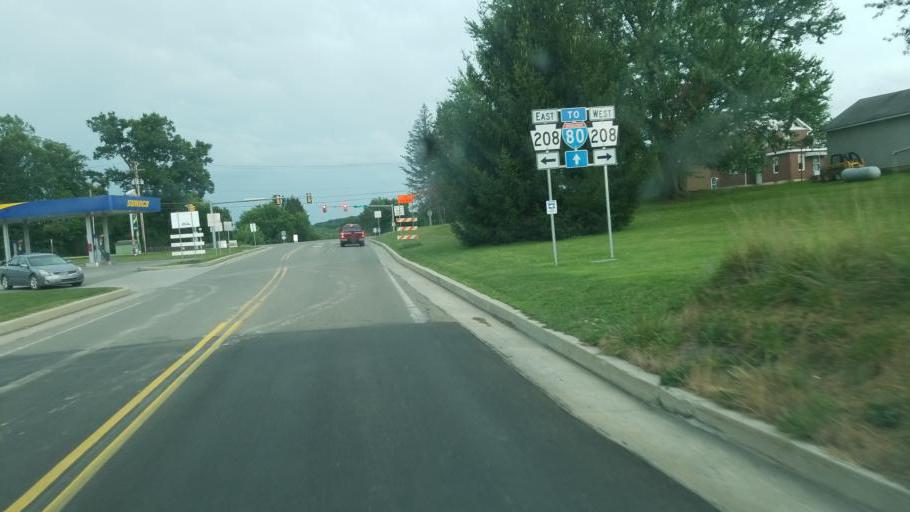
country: US
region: Pennsylvania
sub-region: Clarion County
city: Knox
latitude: 41.2357
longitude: -79.5285
